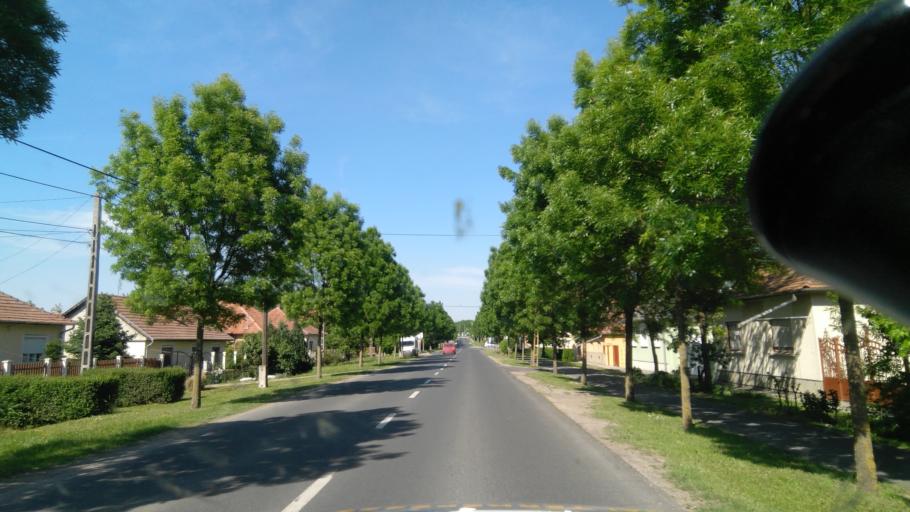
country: HU
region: Bekes
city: Gyula
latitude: 46.6613
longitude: 21.2919
